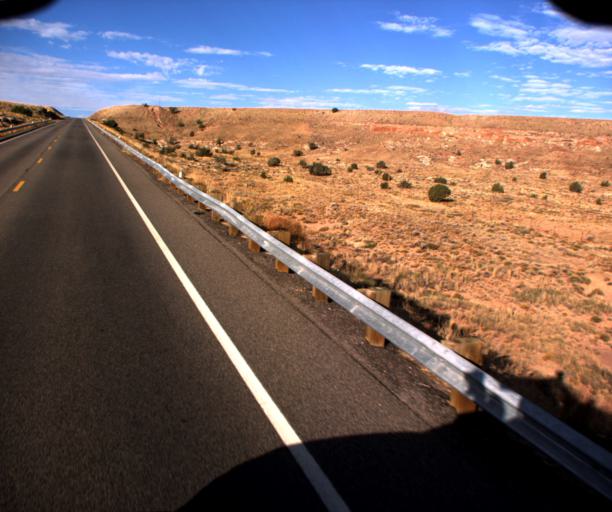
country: US
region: New Mexico
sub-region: San Juan County
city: Shiprock
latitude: 36.9299
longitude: -109.1551
